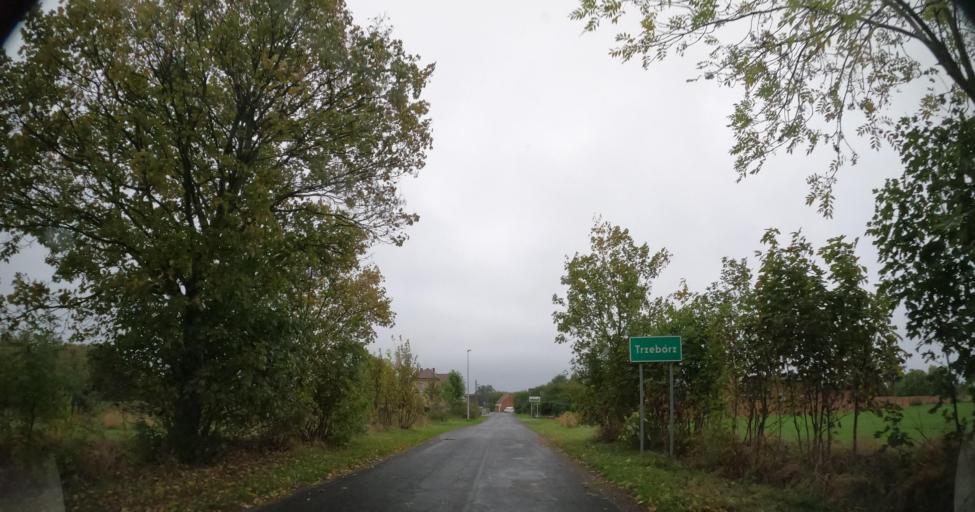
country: PL
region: West Pomeranian Voivodeship
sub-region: Powiat pyrzycki
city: Kozielice
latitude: 53.0746
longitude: 14.7862
